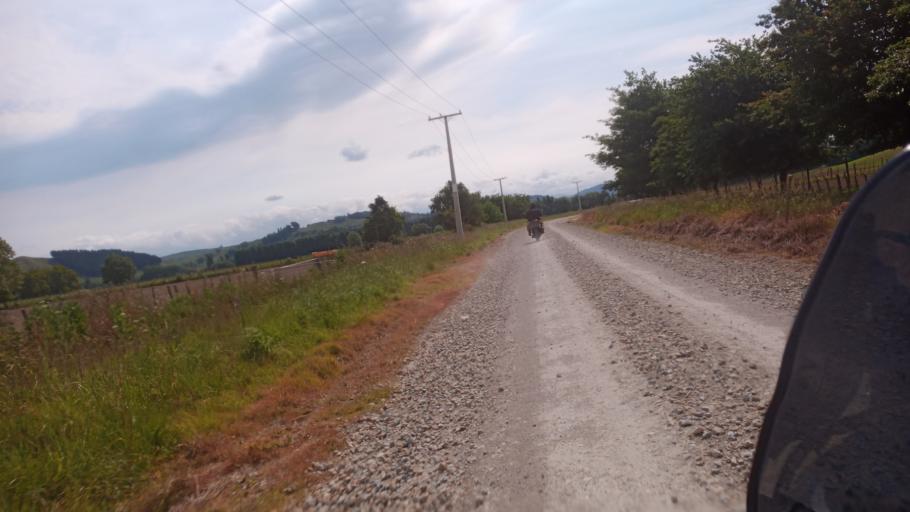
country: NZ
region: Gisborne
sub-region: Gisborne District
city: Gisborne
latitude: -38.4690
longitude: 177.8552
